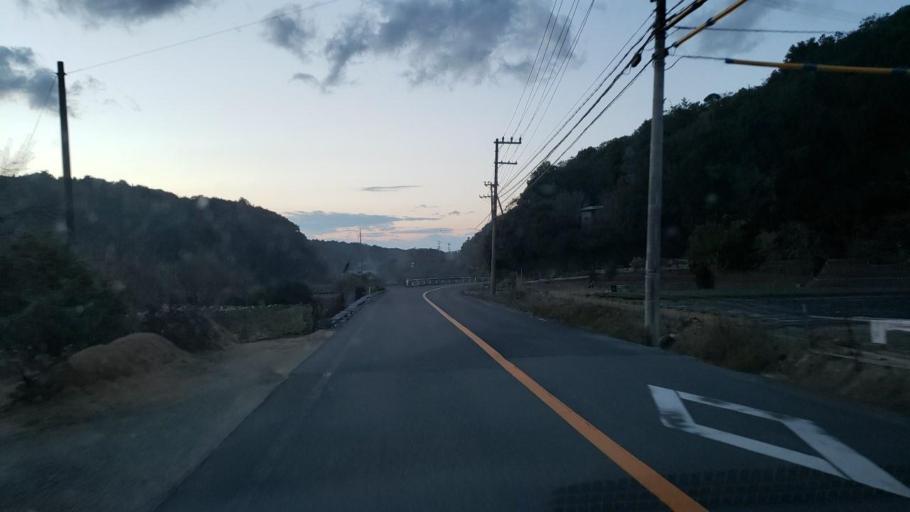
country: JP
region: Hyogo
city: Fukura
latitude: 34.2817
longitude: 134.6969
